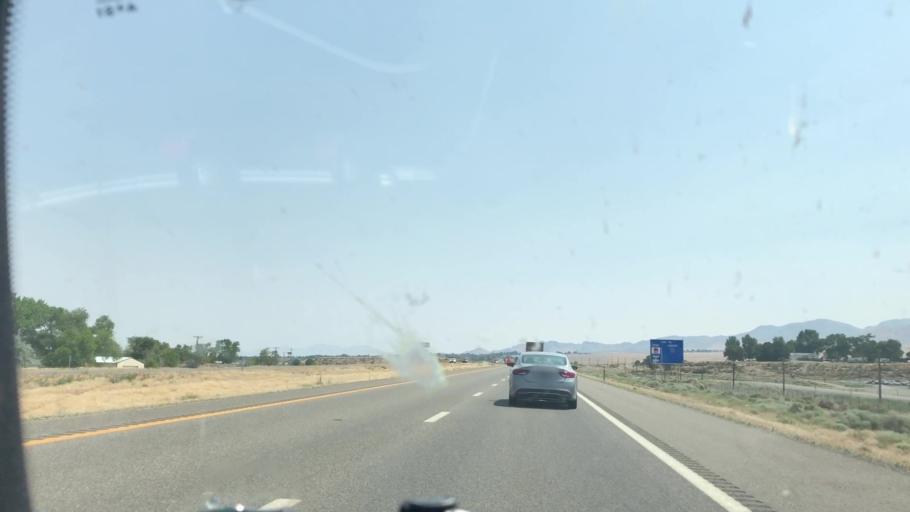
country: US
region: Nevada
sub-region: Humboldt County
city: Winnemucca
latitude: 40.9433
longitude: -117.7727
